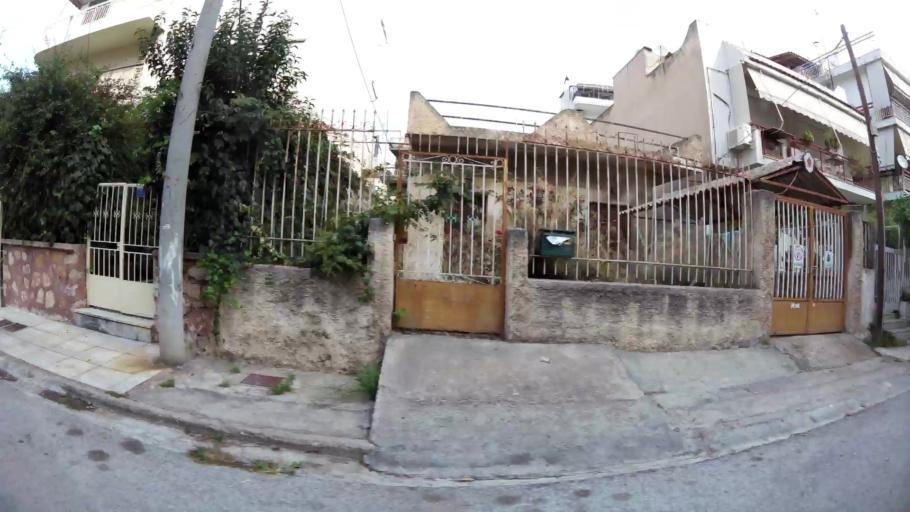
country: GR
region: Attica
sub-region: Nomarchia Athinas
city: Palaio Faliro
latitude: 37.9344
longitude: 23.7038
